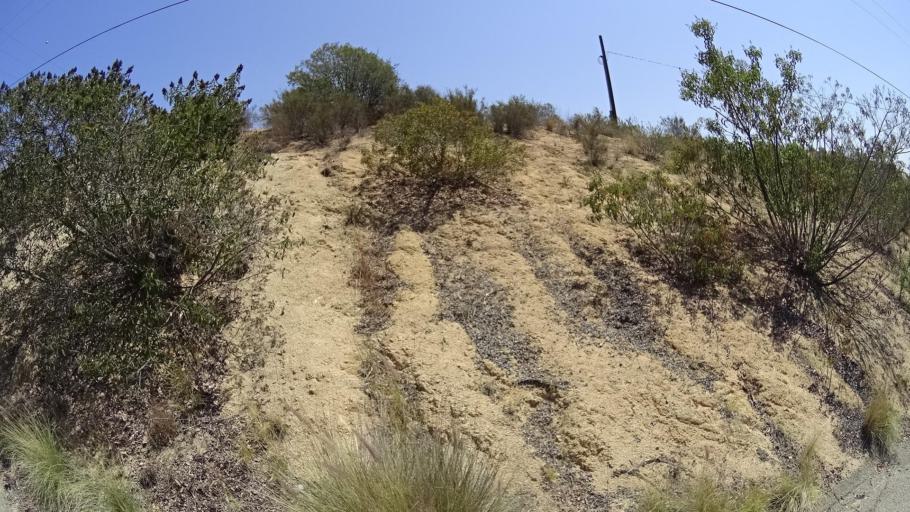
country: US
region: California
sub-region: San Diego County
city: Fallbrook
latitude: 33.4307
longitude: -117.2567
